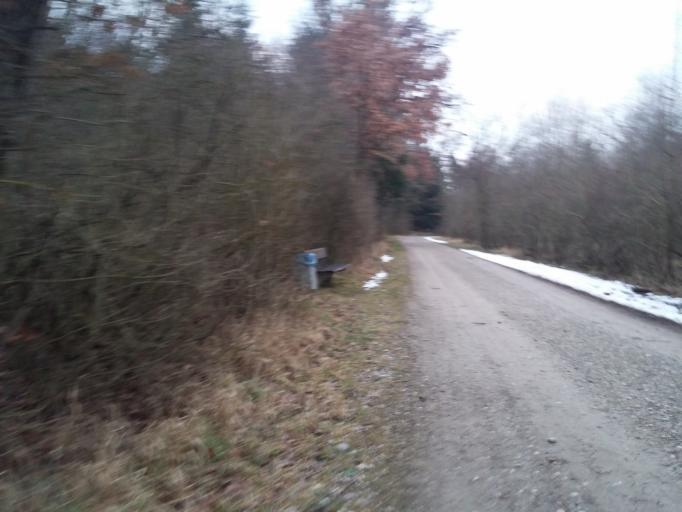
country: DE
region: Bavaria
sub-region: Upper Bavaria
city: Putzbrunn
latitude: 48.0653
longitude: 11.7200
